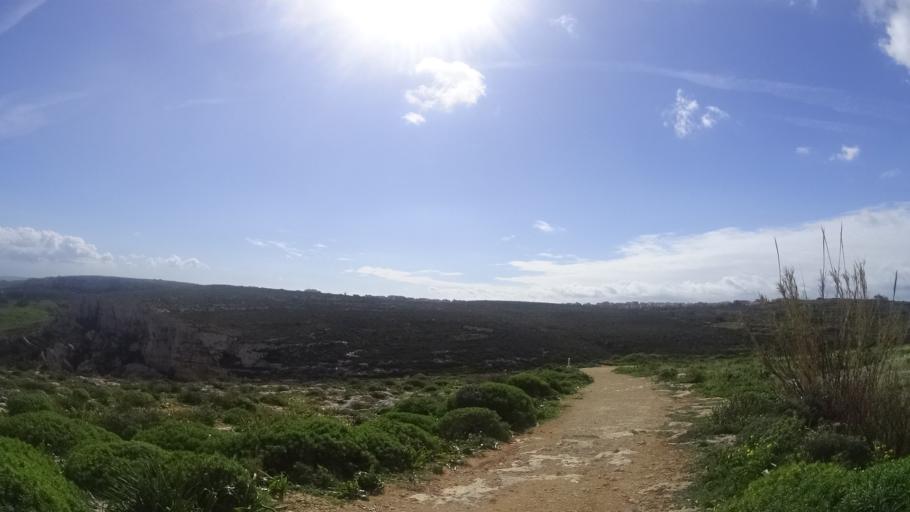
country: MT
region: Il-Qala
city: Qala
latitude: 36.0538
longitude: 14.3084
